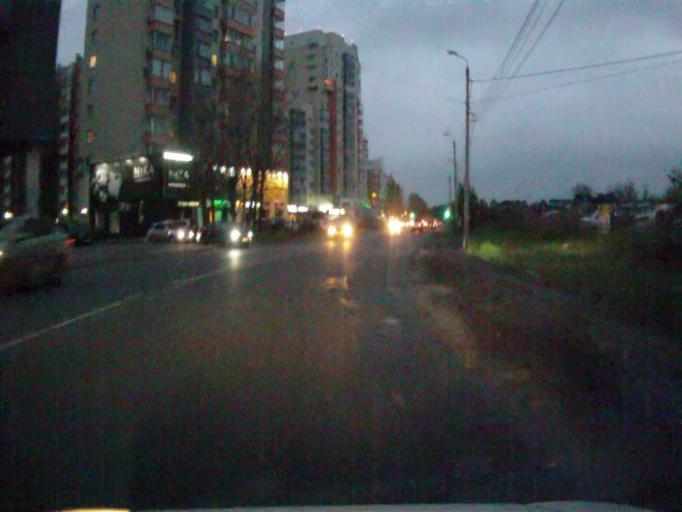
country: RU
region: Chelyabinsk
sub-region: Gorod Chelyabinsk
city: Chelyabinsk
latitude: 55.1618
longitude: 61.2959
